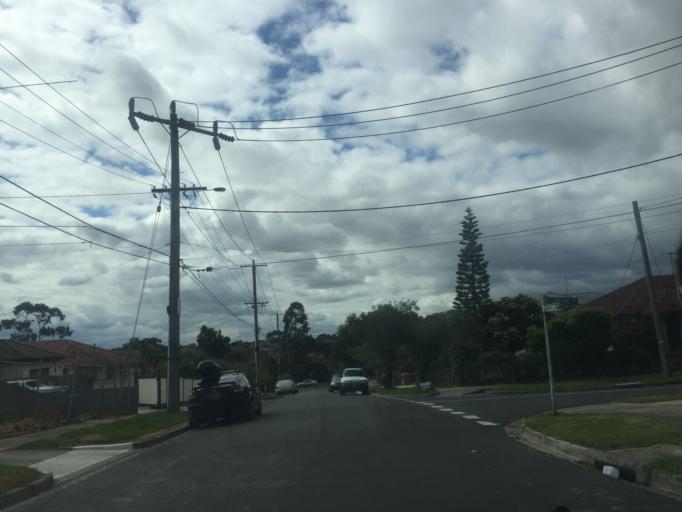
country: AU
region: Victoria
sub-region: Darebin
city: Reservoir
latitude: -37.7191
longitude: 145.0161
